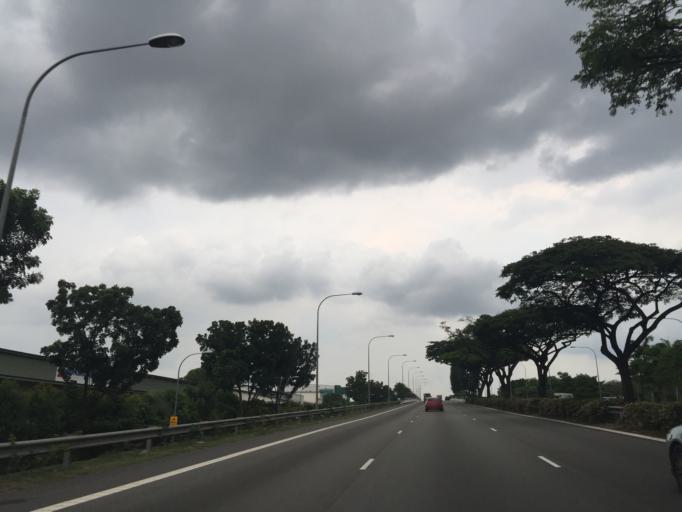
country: SG
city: Singapore
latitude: 1.3219
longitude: 103.7060
